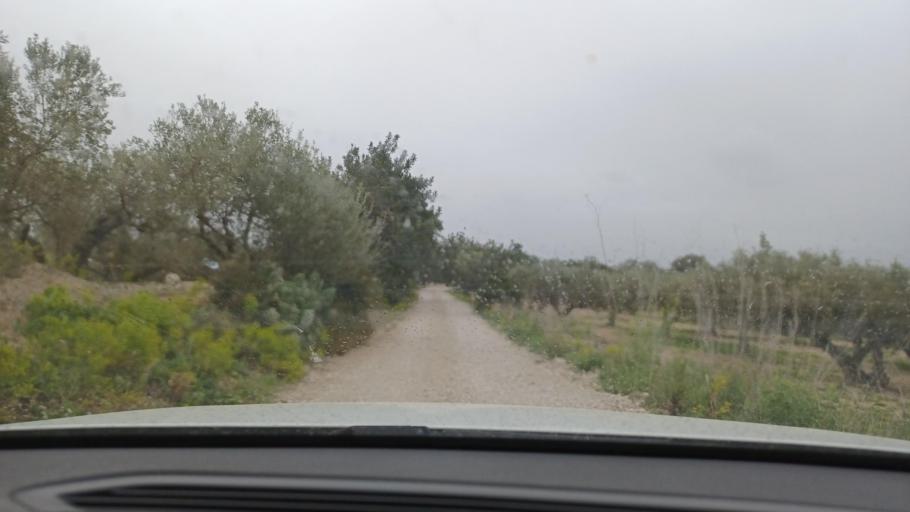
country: ES
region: Catalonia
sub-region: Provincia de Tarragona
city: Mas de Barberans
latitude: 40.8036
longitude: 0.4120
